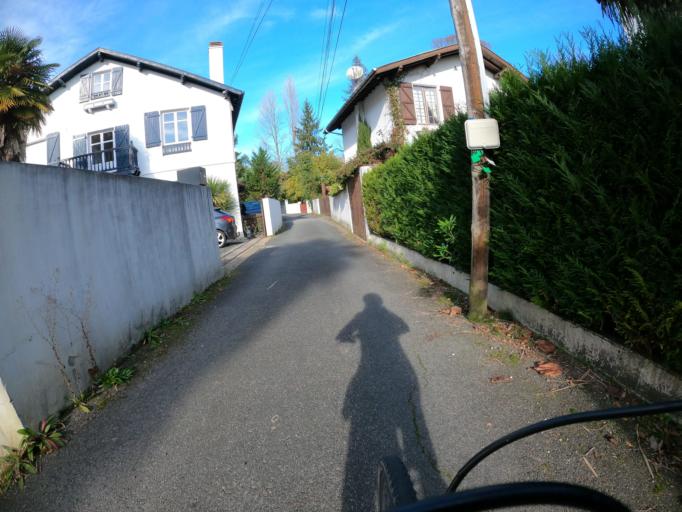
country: FR
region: Aquitaine
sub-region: Departement des Pyrenees-Atlantiques
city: Bayonne
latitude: 43.4983
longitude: -1.4643
